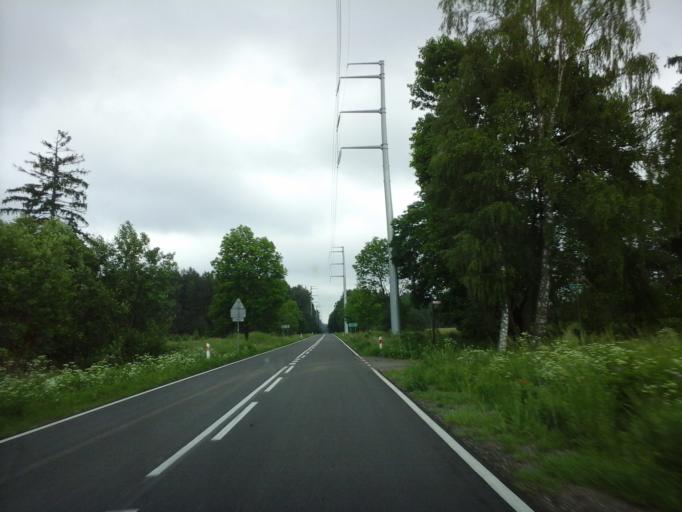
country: PL
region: West Pomeranian Voivodeship
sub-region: Powiat drawski
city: Czaplinek
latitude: 53.4853
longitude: 16.2291
